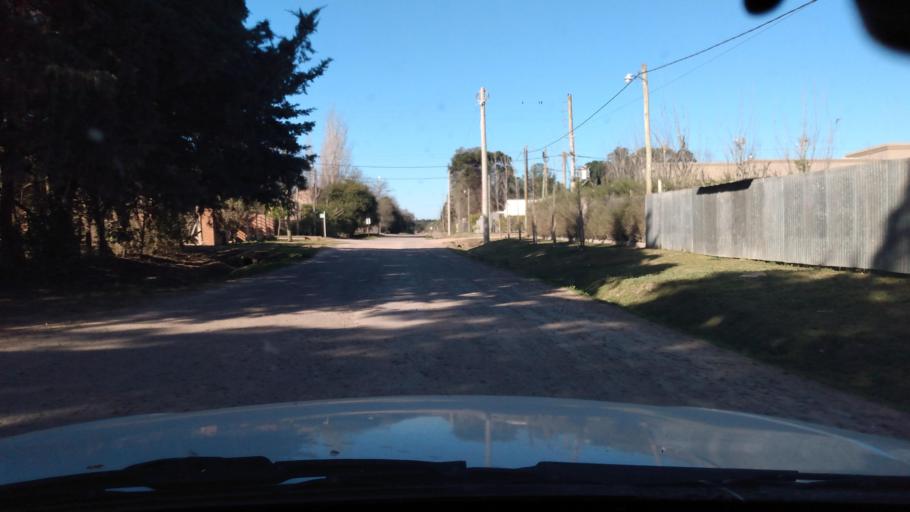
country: AR
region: Buenos Aires
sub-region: Partido de Mercedes
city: Mercedes
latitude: -34.6486
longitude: -59.4012
